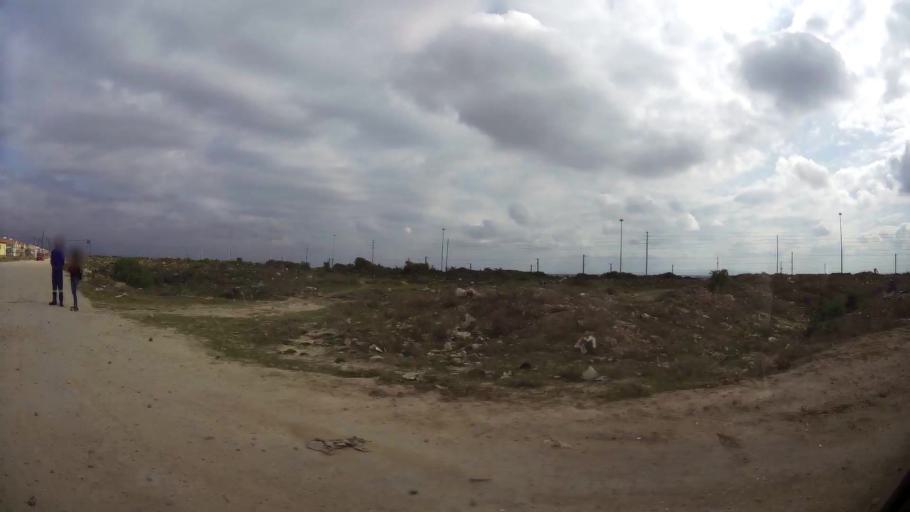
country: ZA
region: Eastern Cape
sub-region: Nelson Mandela Bay Metropolitan Municipality
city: Port Elizabeth
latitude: -33.8248
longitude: 25.6232
